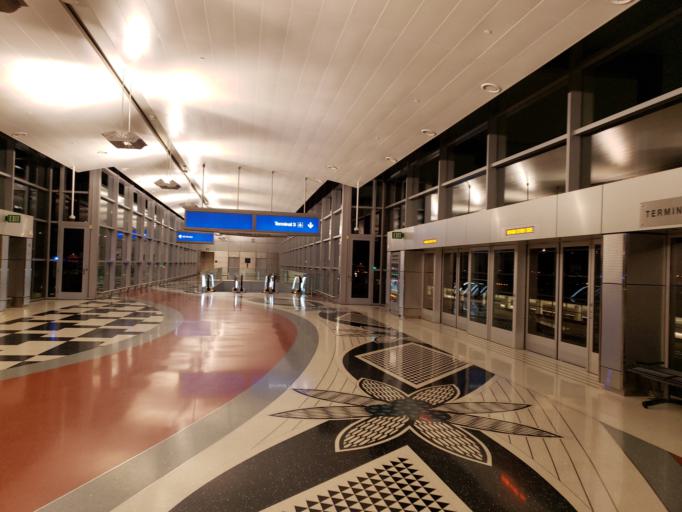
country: US
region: Arizona
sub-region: Maricopa County
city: Phoenix
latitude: 33.4348
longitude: -112.0102
